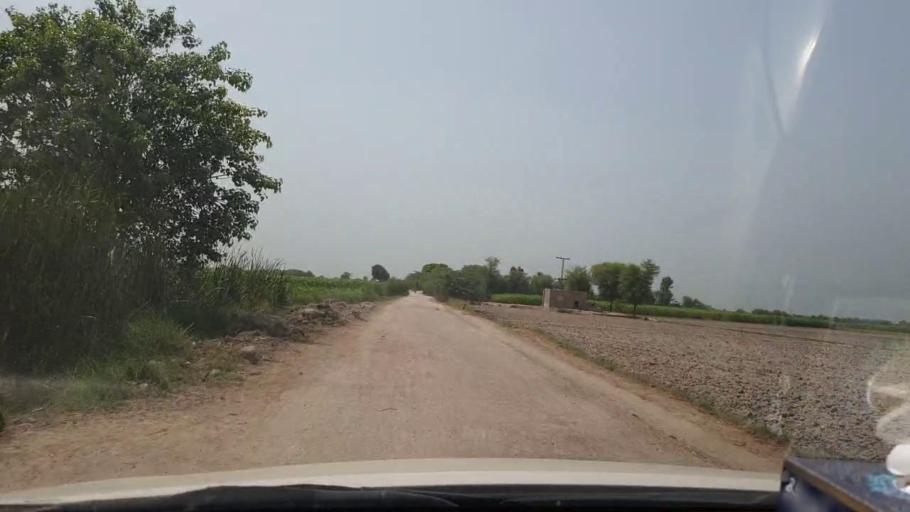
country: PK
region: Sindh
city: Shikarpur
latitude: 27.9940
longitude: 68.7127
